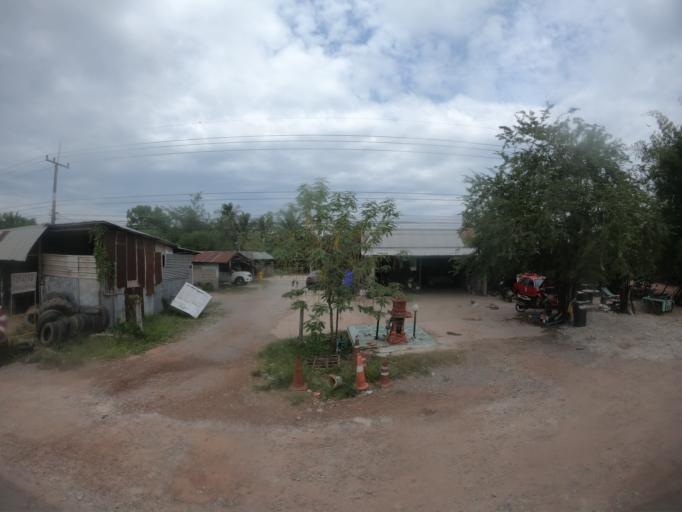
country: TH
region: Maha Sarakham
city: Kantharawichai
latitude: 16.3281
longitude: 103.2838
